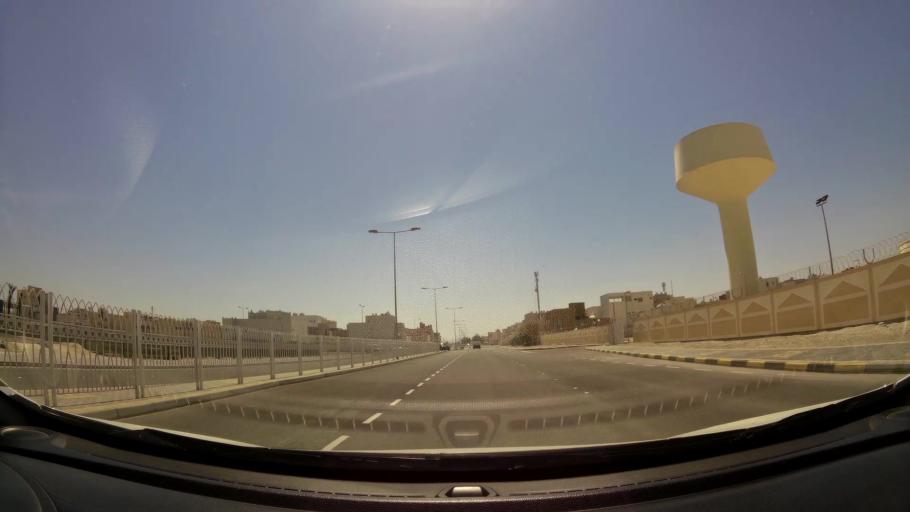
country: BH
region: Muharraq
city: Al Hadd
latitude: 26.2810
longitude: 50.6435
